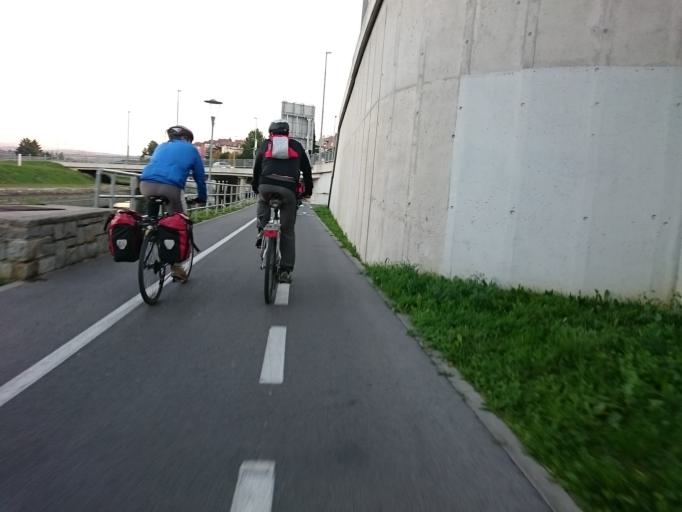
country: SI
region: Koper-Capodistria
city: Koper
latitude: 45.5404
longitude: 13.7207
